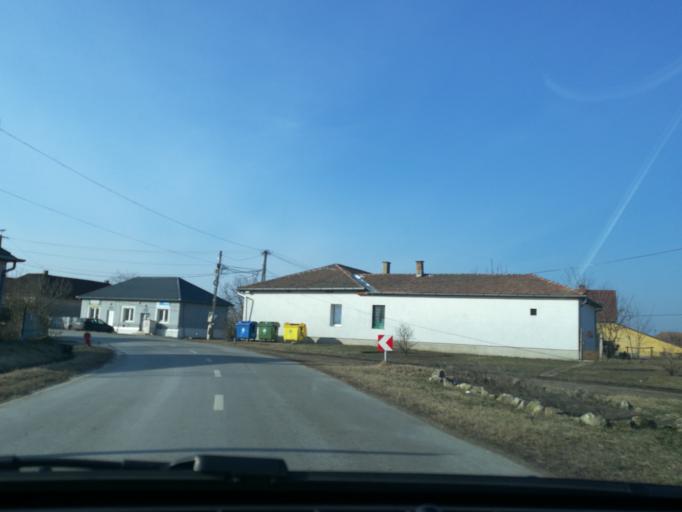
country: HU
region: Szabolcs-Szatmar-Bereg
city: Apagy
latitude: 48.0252
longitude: 21.9607
